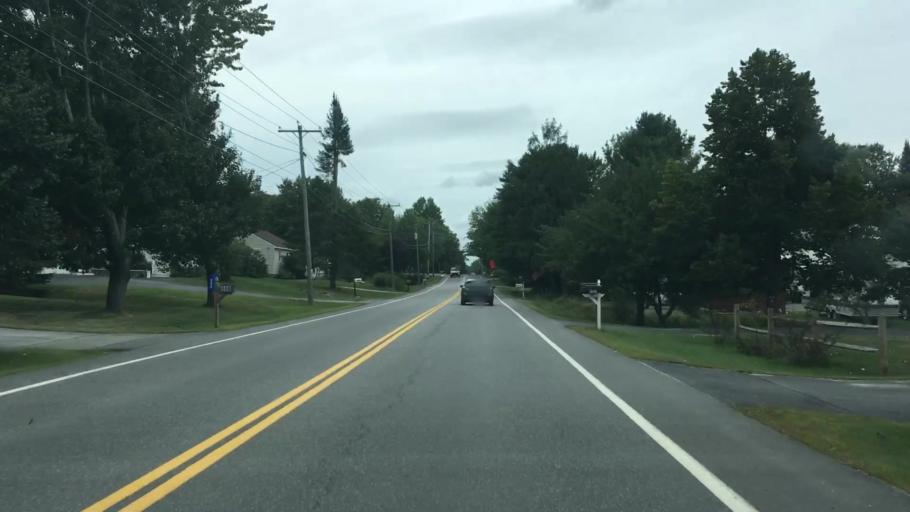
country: US
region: Maine
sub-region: Cumberland County
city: Yarmouth
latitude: 43.8209
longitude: -70.1880
